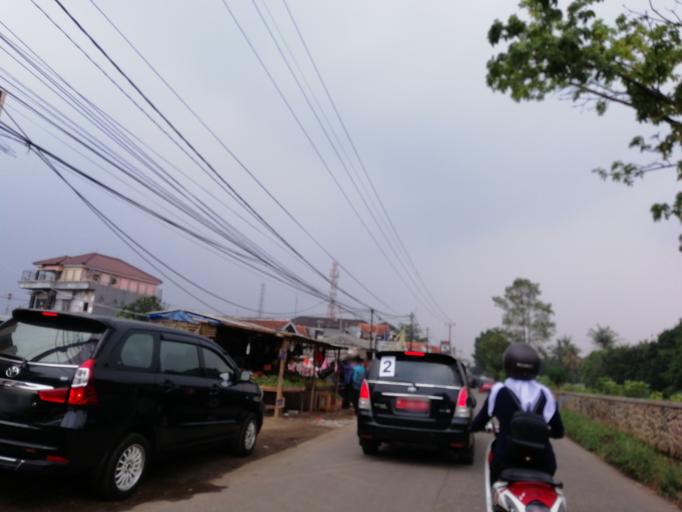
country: ID
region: West Java
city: Cibinong
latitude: -6.4763
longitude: 106.8035
